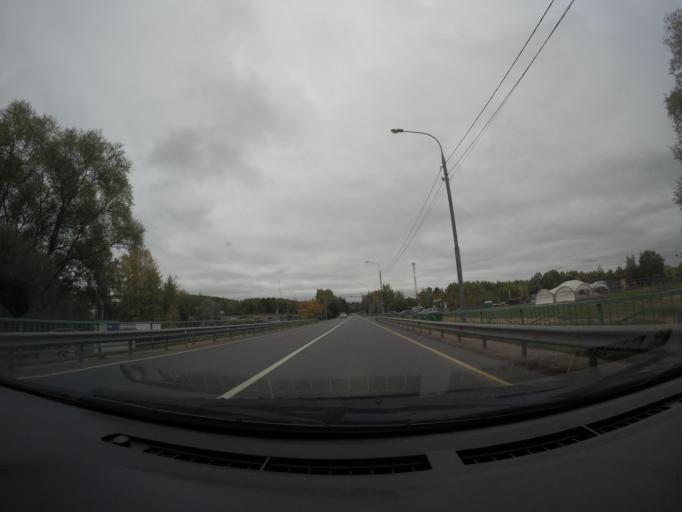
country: RU
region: Moskovskaya
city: Ruza
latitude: 55.7591
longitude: 36.2603
